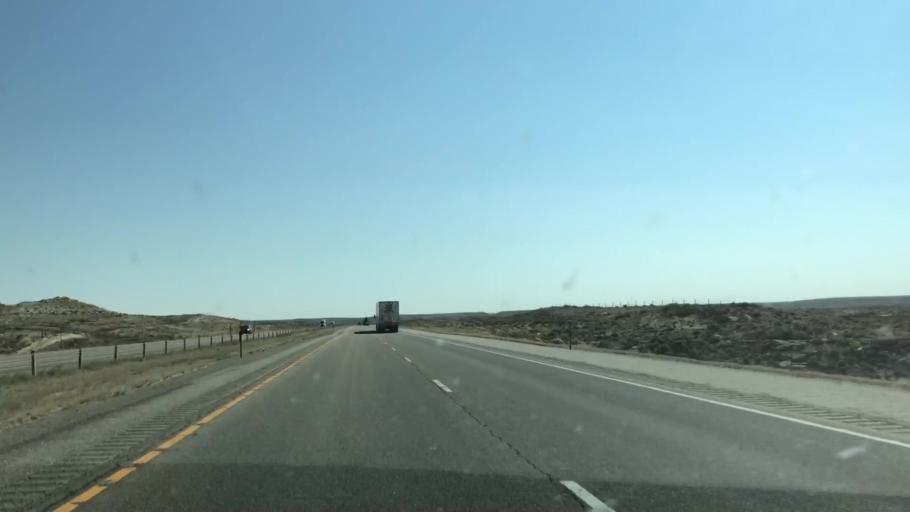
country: US
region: Wyoming
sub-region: Sweetwater County
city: Rock Springs
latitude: 41.6469
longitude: -108.6404
